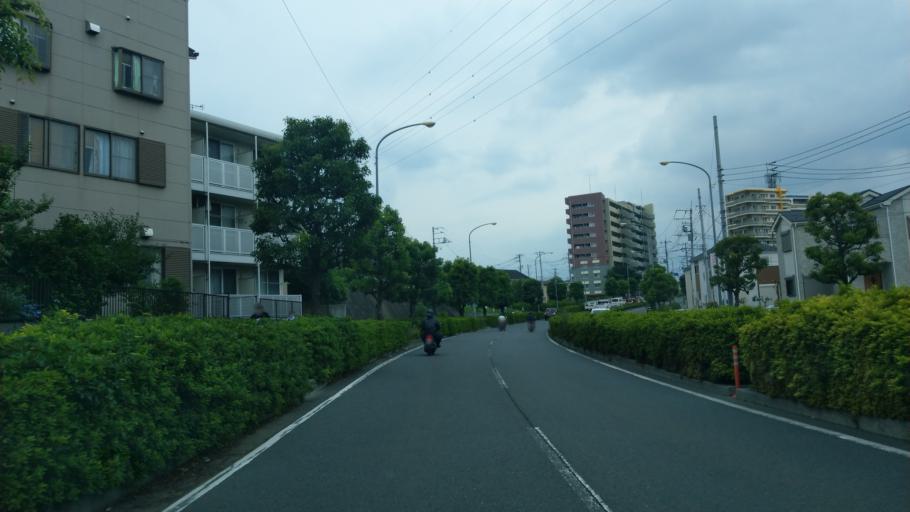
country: JP
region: Saitama
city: Shimotoda
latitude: 35.8558
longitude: 139.6921
